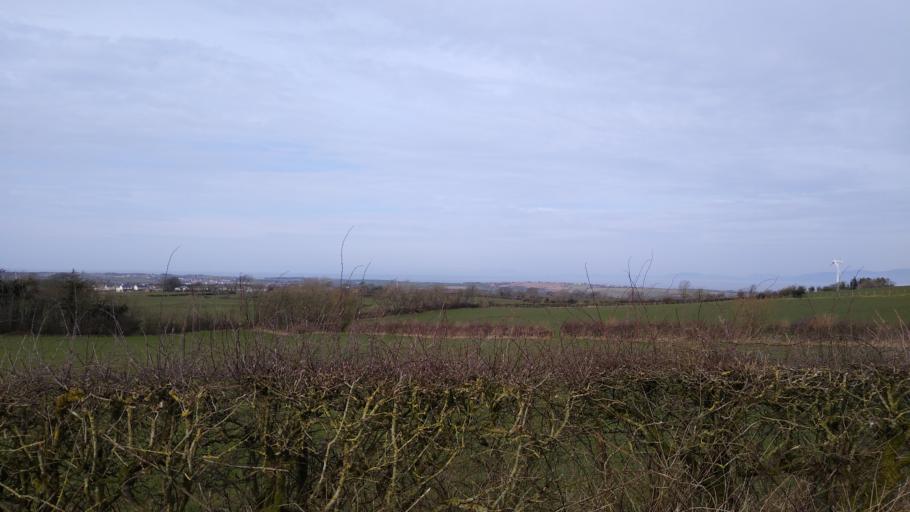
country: GB
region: England
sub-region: Cumbria
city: Cockermouth
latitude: 54.7053
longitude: -3.3694
